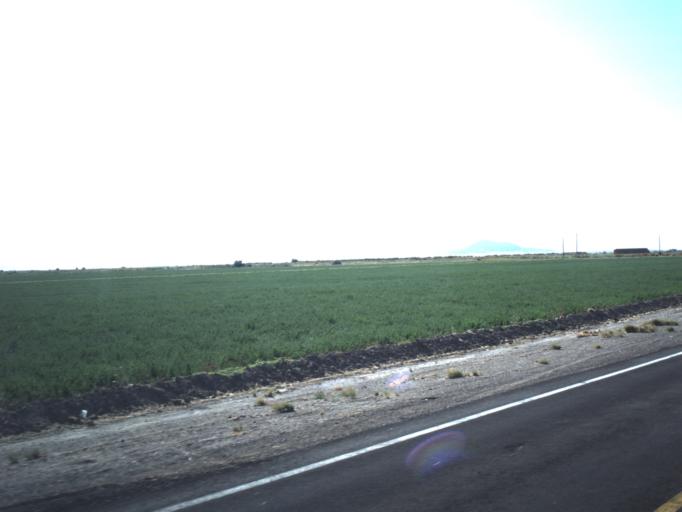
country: US
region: Utah
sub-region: Millard County
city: Delta
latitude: 39.2825
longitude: -112.6529
